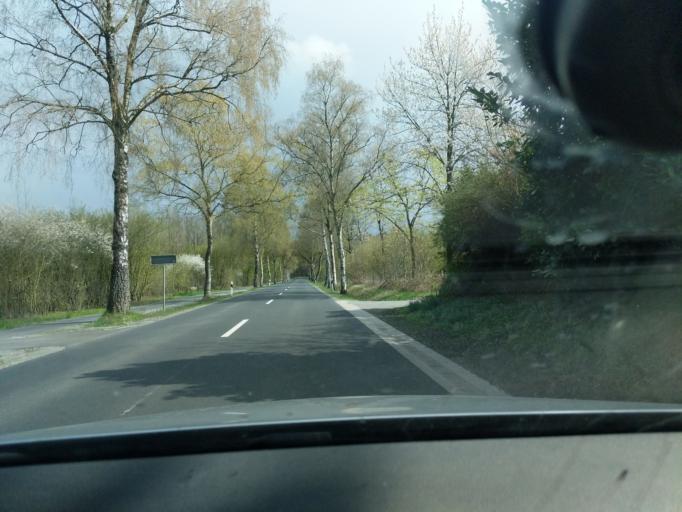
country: DE
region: Lower Saxony
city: Dollern
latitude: 53.5185
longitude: 9.5103
